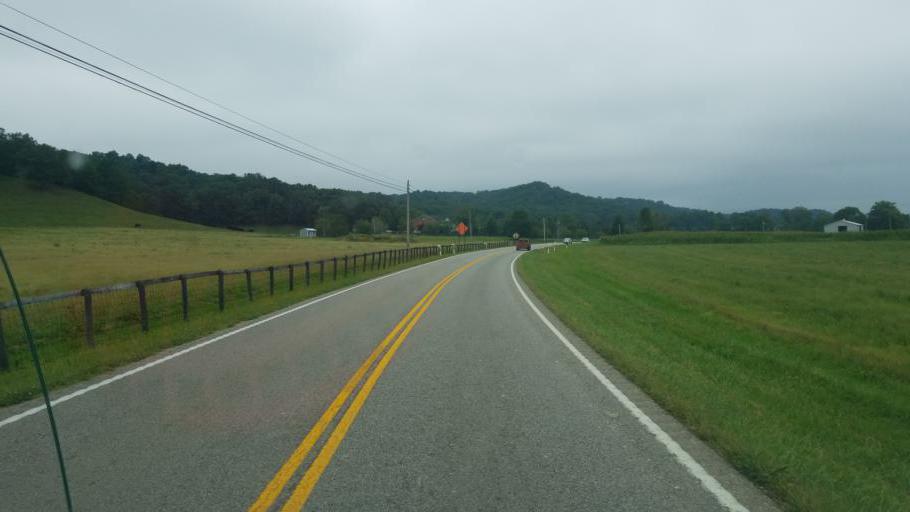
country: US
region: Kentucky
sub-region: Rowan County
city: Morehead
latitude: 38.2172
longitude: -83.4720
